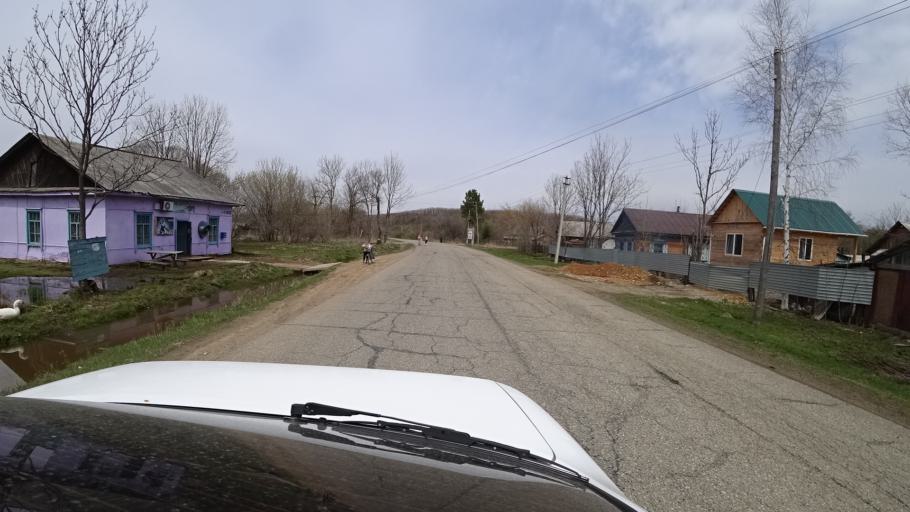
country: RU
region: Primorskiy
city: Novopokrovka
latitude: 45.7879
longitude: 134.1145
